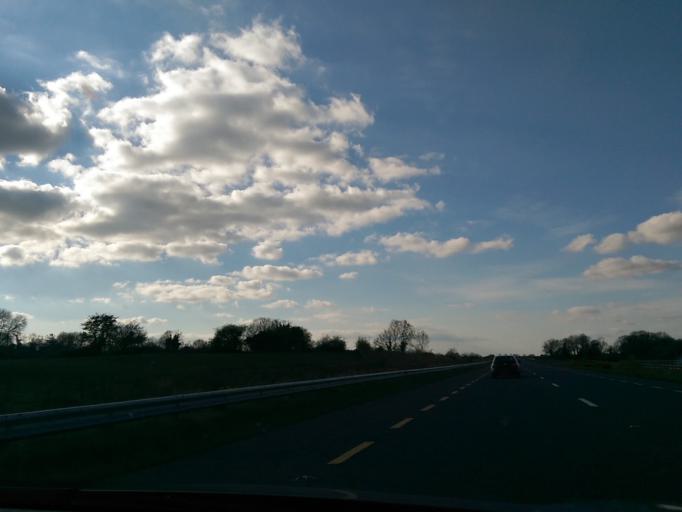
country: IE
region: Connaught
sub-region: County Galway
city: Loughrea
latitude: 53.2240
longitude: -8.5862
